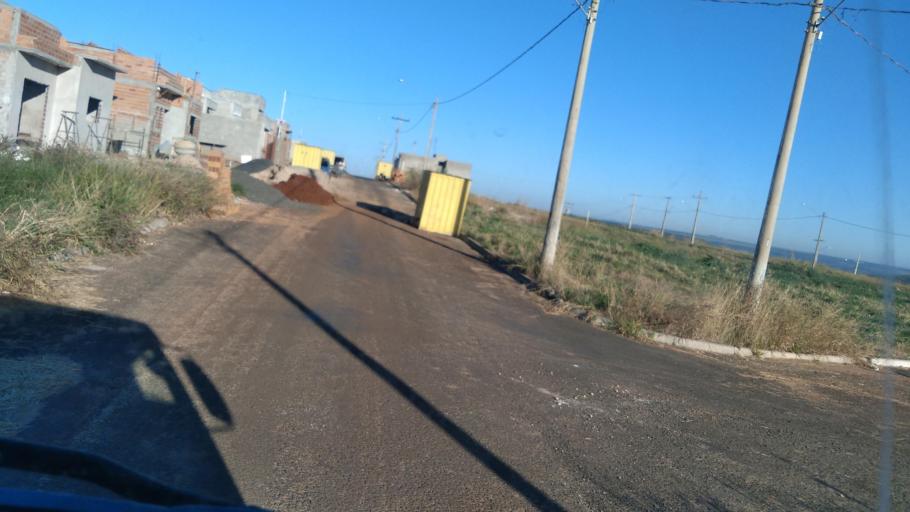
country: BR
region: Goias
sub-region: Mineiros
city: Mineiros
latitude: -17.5414
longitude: -52.5538
